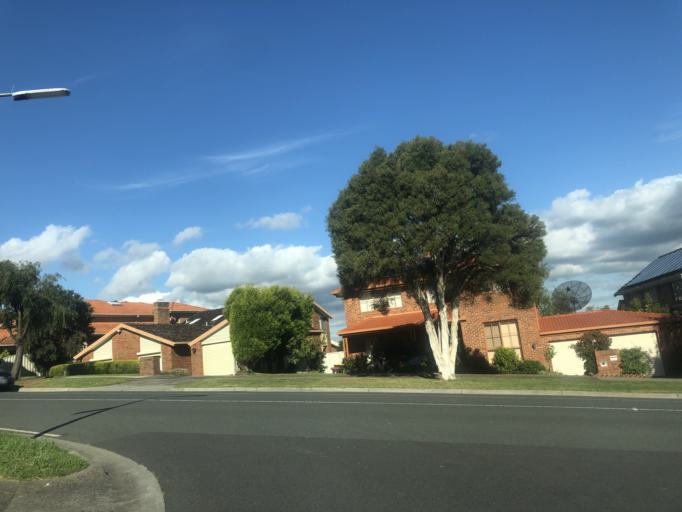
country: AU
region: Victoria
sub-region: Monash
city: Mulgrave
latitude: -37.9169
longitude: 145.1930
